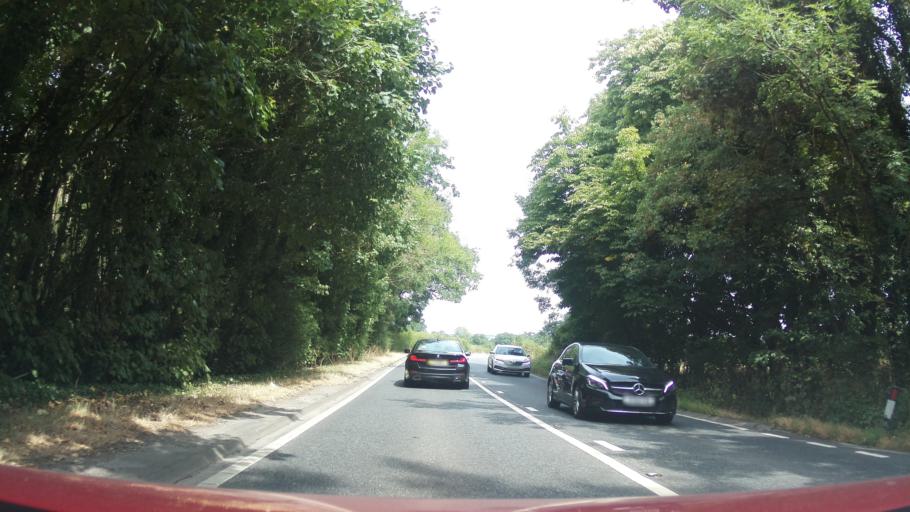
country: GB
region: England
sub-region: Surrey
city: Salfords
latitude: 51.2000
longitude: -0.1983
